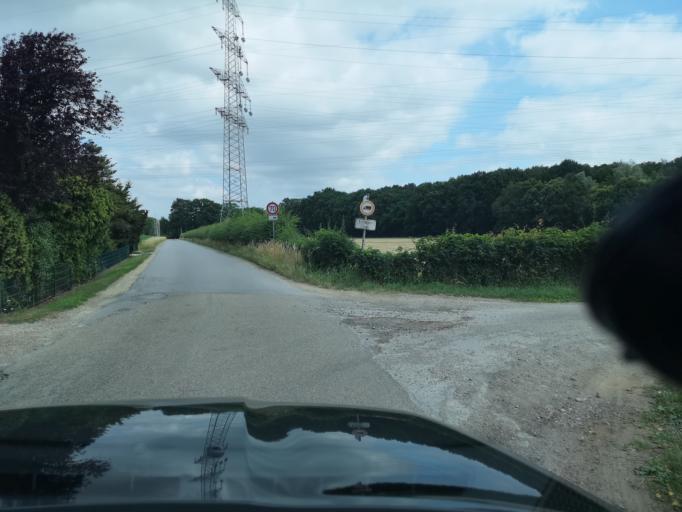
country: DE
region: North Rhine-Westphalia
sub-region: Regierungsbezirk Dusseldorf
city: Wesel
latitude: 51.6946
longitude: 6.6324
